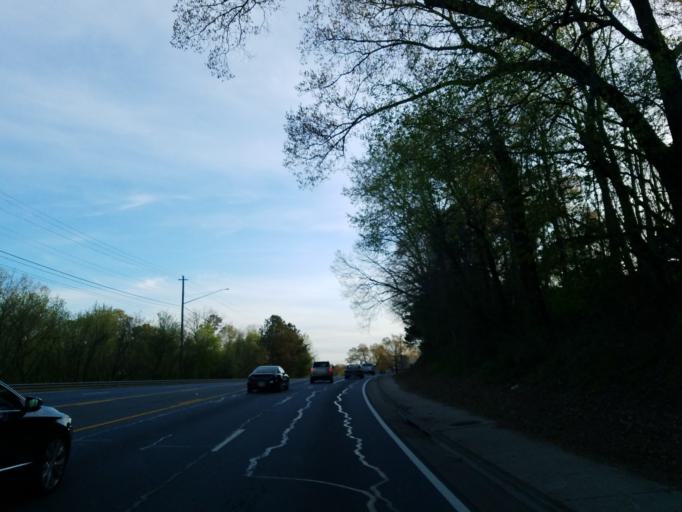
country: US
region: Georgia
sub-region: Cherokee County
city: Canton
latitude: 34.2396
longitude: -84.4985
